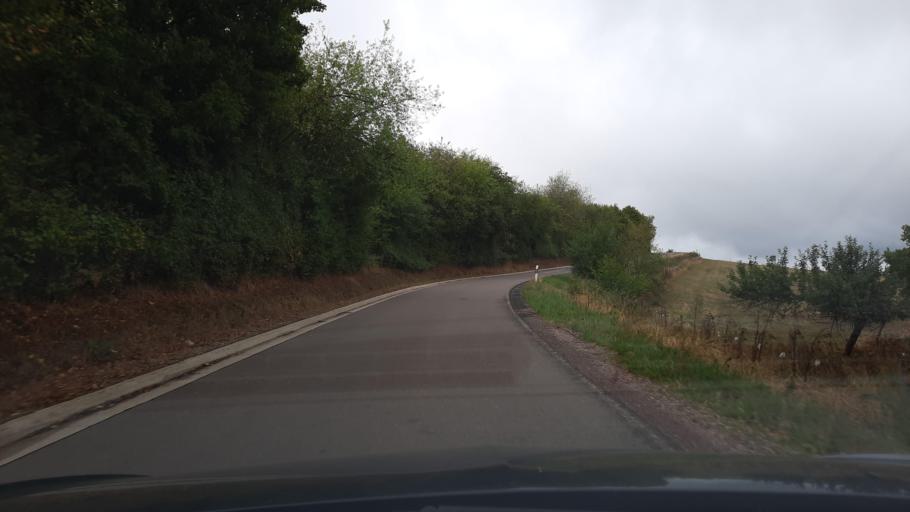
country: DE
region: Rheinland-Pfalz
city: Zerf
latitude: 49.6016
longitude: 6.6489
